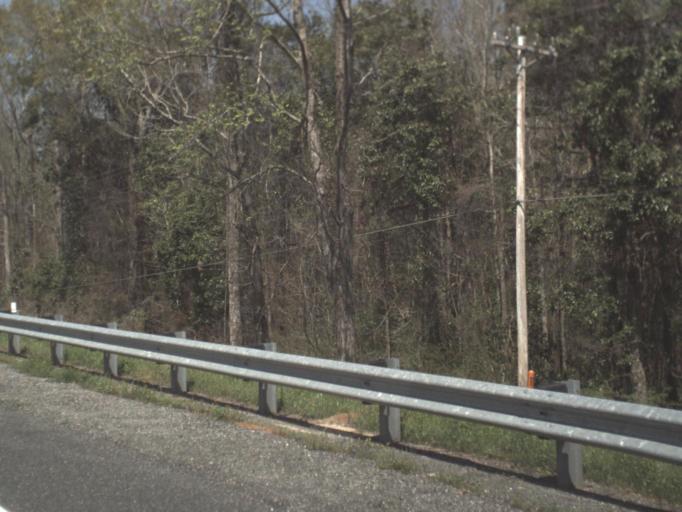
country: US
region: Florida
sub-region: Gadsden County
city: Midway
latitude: 30.5316
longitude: -84.4734
